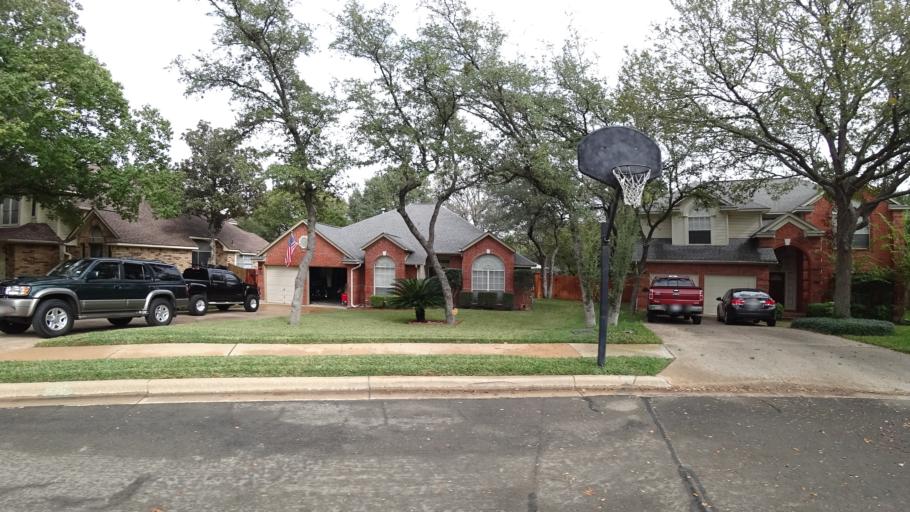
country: US
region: Texas
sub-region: Williamson County
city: Brushy Creek
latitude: 30.5170
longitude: -97.7172
